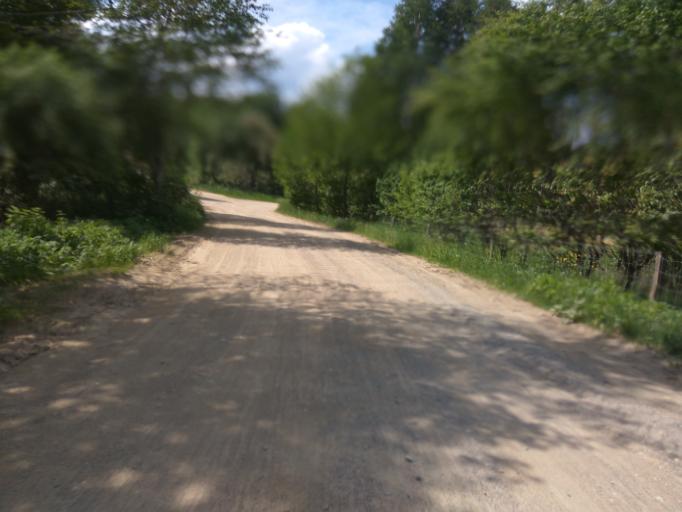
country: LV
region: Kuldigas Rajons
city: Kuldiga
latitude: 56.8829
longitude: 21.9332
